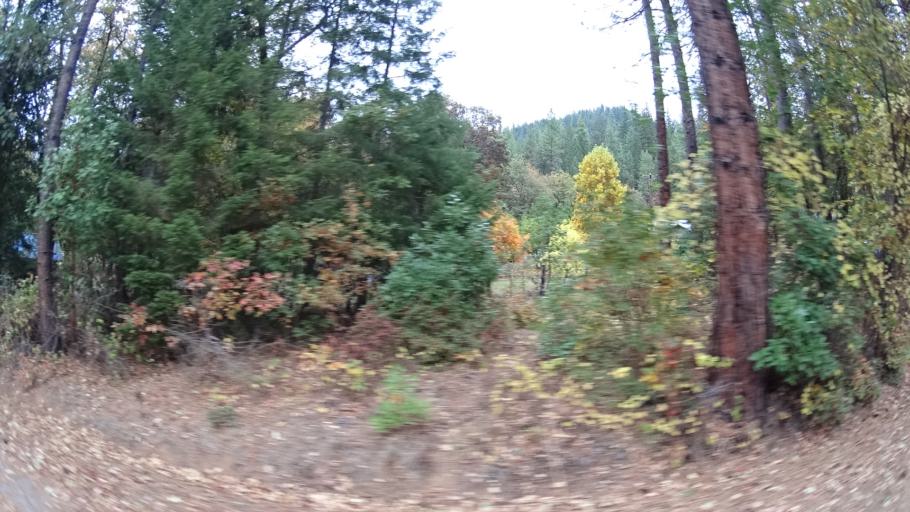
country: US
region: California
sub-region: Siskiyou County
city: Happy Camp
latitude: 41.8369
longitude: -123.1840
